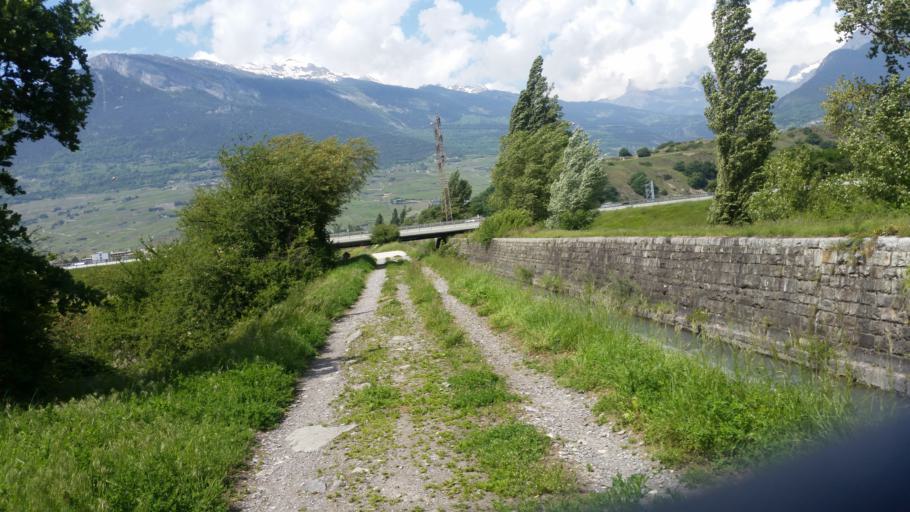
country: CH
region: Valais
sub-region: Conthey District
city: Conthey
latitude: 46.2119
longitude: 7.3077
